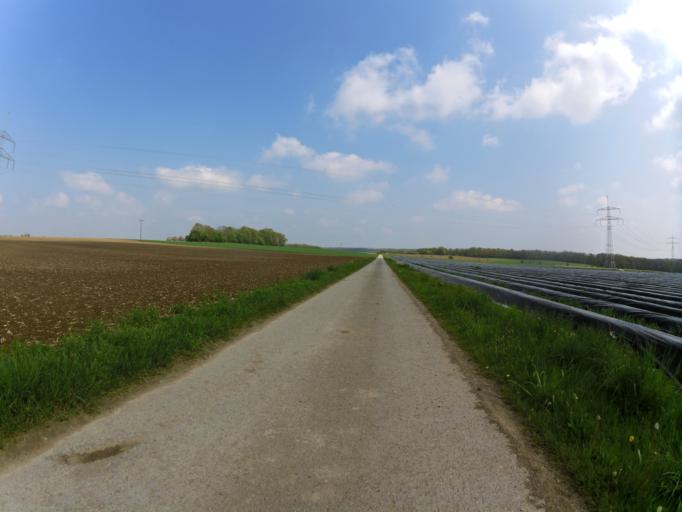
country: DE
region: Bavaria
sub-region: Regierungsbezirk Unterfranken
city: Sommerhausen
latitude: 49.7092
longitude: 10.0614
